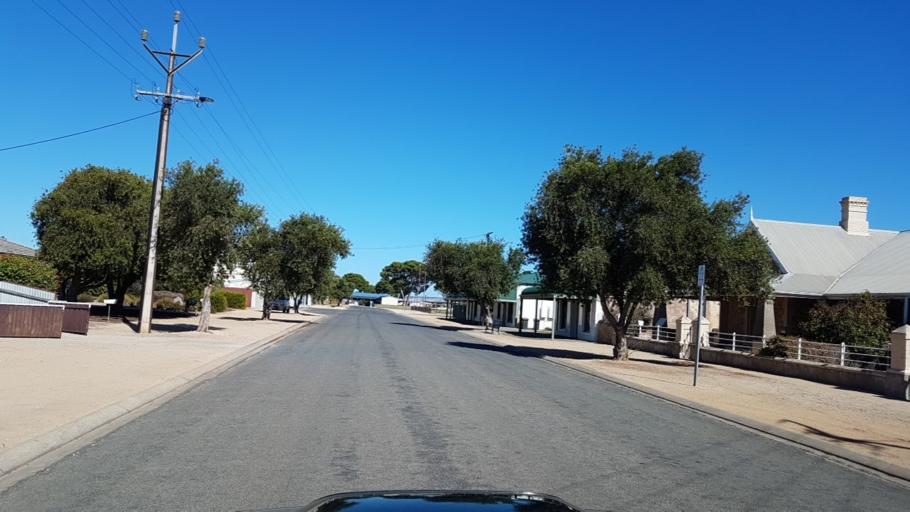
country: AU
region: South Australia
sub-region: Wakefield
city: Balaklava
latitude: -34.1863
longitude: 138.1479
